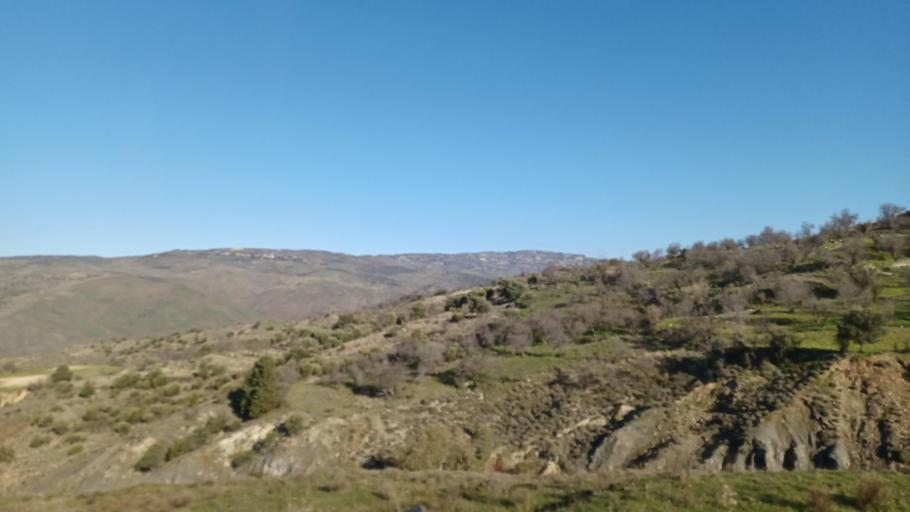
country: CY
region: Limassol
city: Pachna
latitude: 34.8166
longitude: 32.6523
